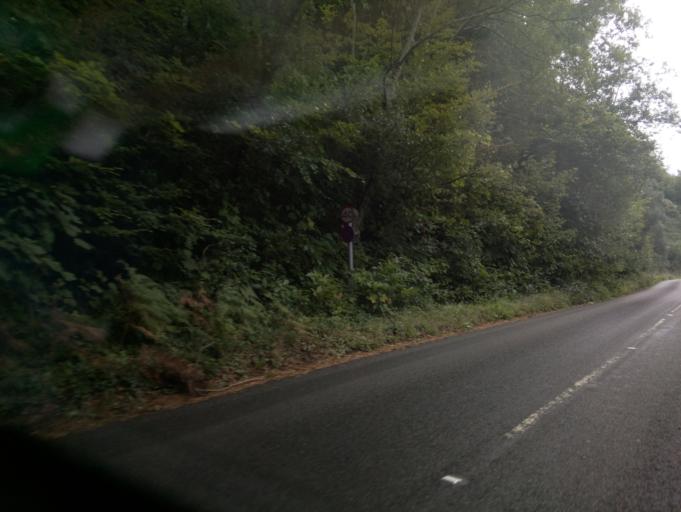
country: GB
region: England
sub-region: Devon
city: Dartmouth
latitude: 50.3208
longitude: -3.6064
